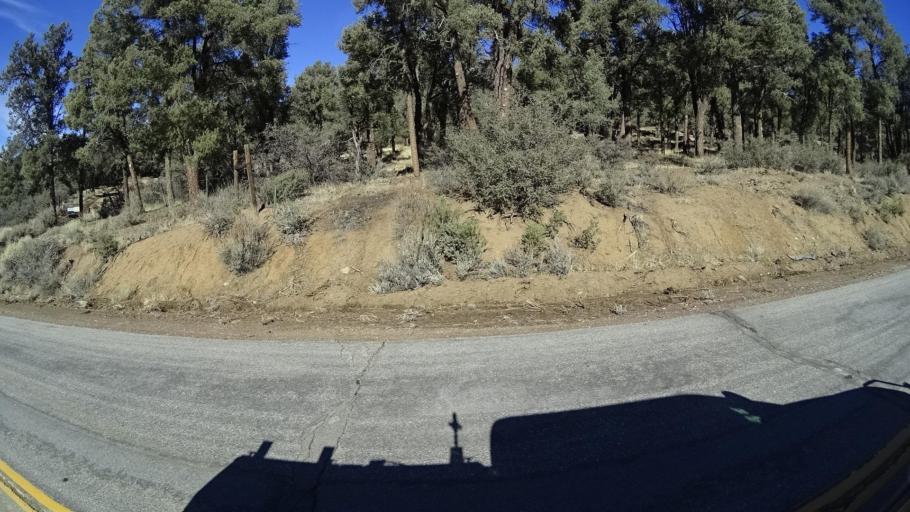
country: US
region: California
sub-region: Kern County
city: Pine Mountain Club
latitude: 34.8615
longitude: -119.2125
